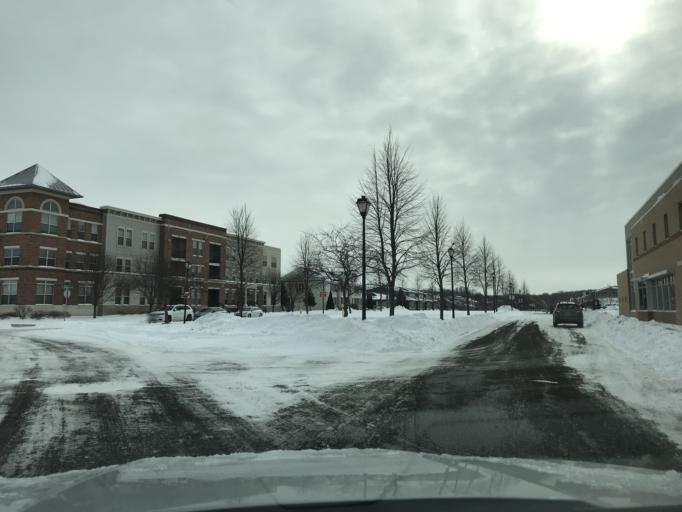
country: US
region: Wisconsin
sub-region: Dane County
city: Sun Prairie
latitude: 43.1617
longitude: -89.2626
